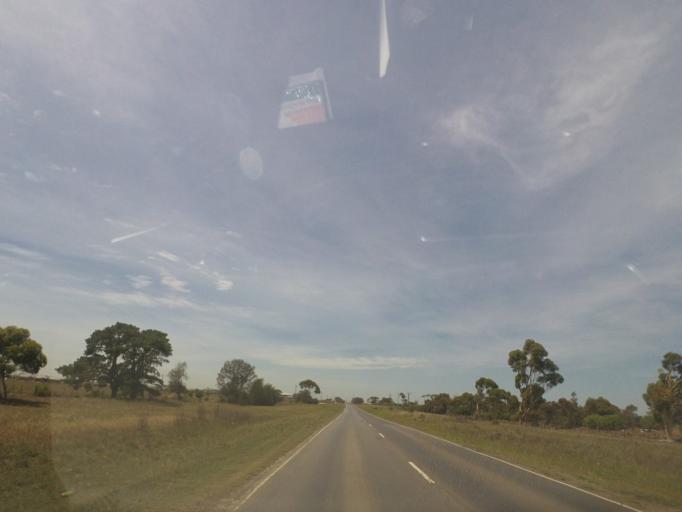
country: AU
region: Victoria
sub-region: Wyndham
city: Wyndham Vale
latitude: -37.8502
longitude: 144.5816
